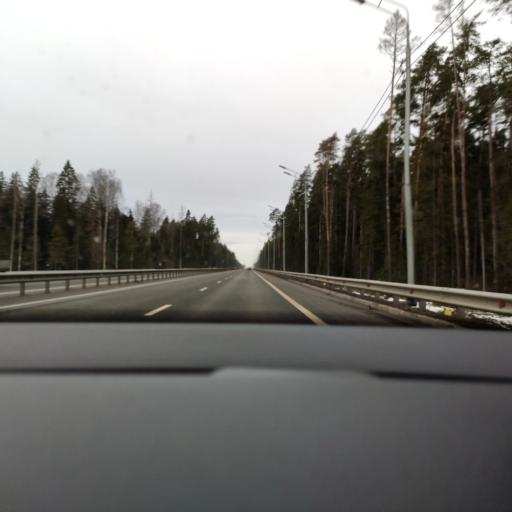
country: RU
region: Moskovskaya
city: Bol'shiye Vyazemy
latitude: 55.6669
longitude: 36.9328
